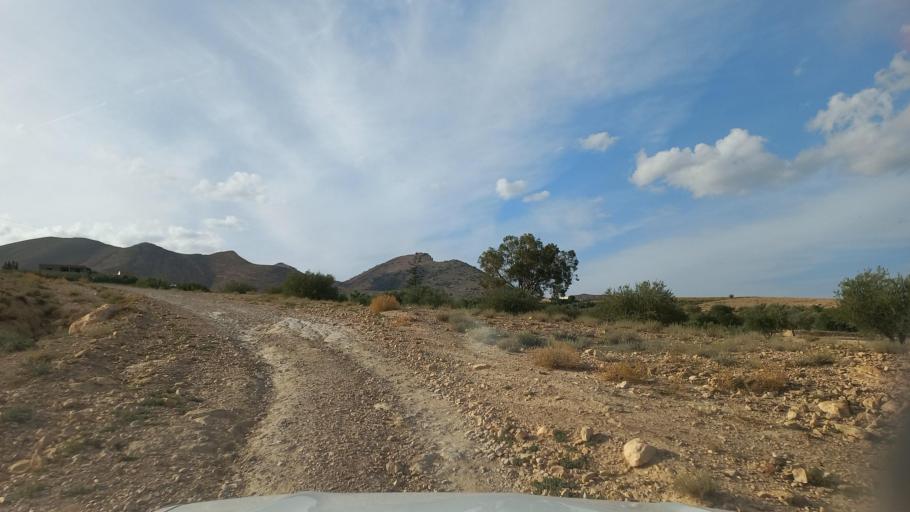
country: TN
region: Al Qasrayn
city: Sbiba
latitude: 35.4536
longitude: 9.0831
